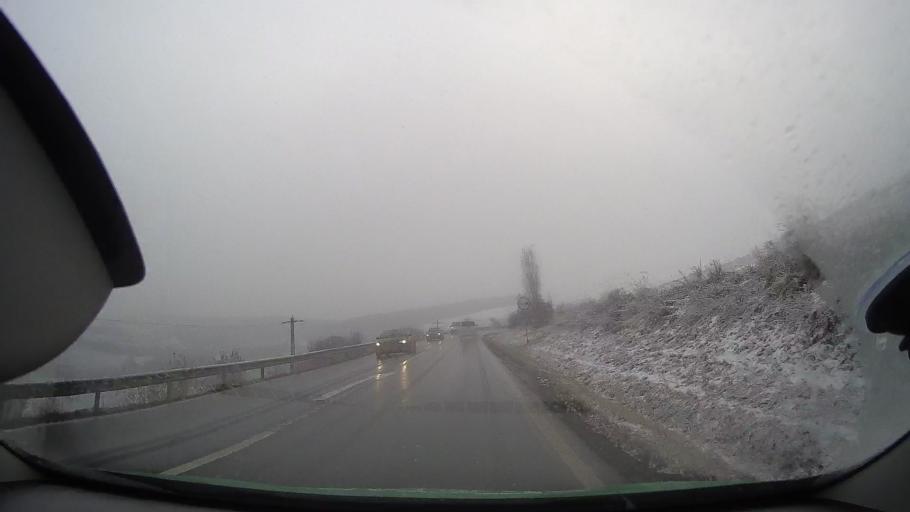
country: RO
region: Mures
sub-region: Comuna Bagaciu
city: Delenii
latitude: 46.2635
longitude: 24.3015
